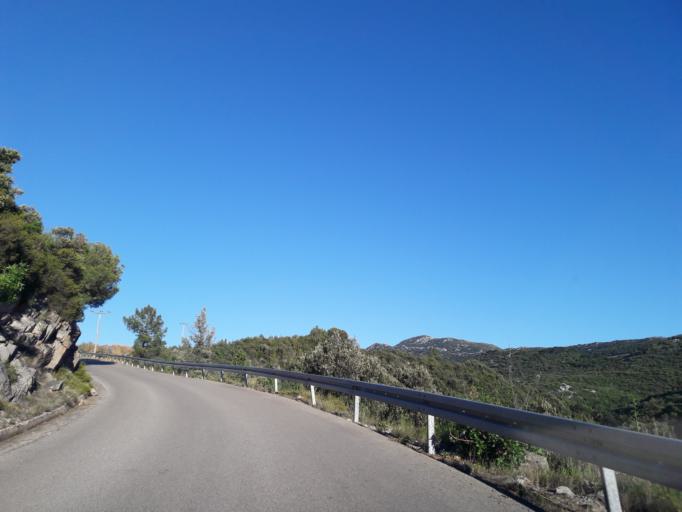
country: HR
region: Dubrovacko-Neretvanska
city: Orebic
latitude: 43.0109
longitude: 17.2046
